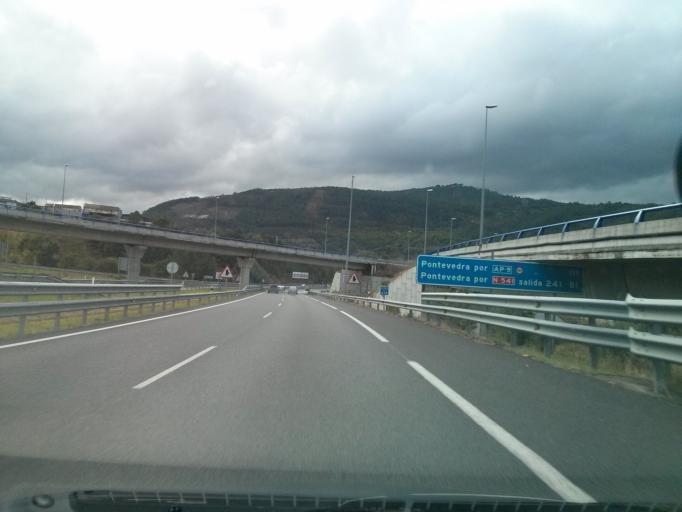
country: ES
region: Galicia
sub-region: Provincia de Ourense
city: Punxin
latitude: 42.3408
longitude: -7.9938
